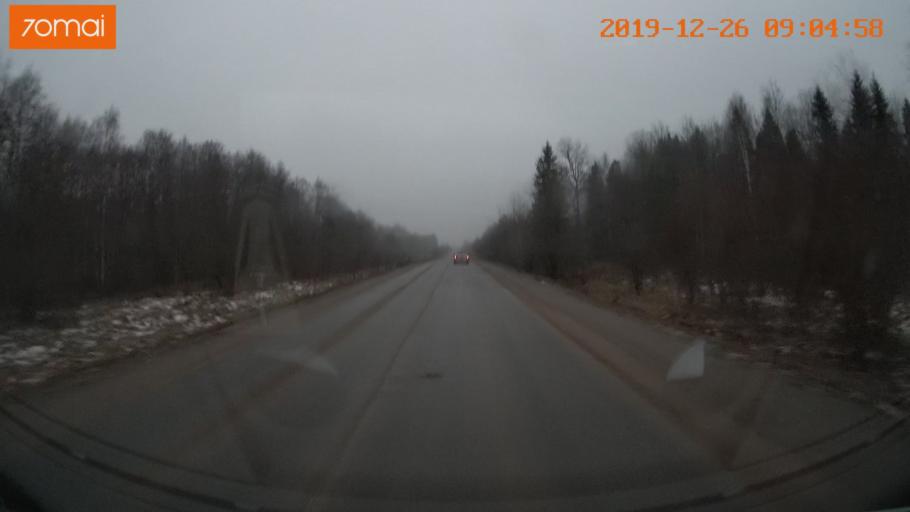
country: RU
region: Vologda
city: Gryazovets
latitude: 58.8209
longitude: 40.2601
